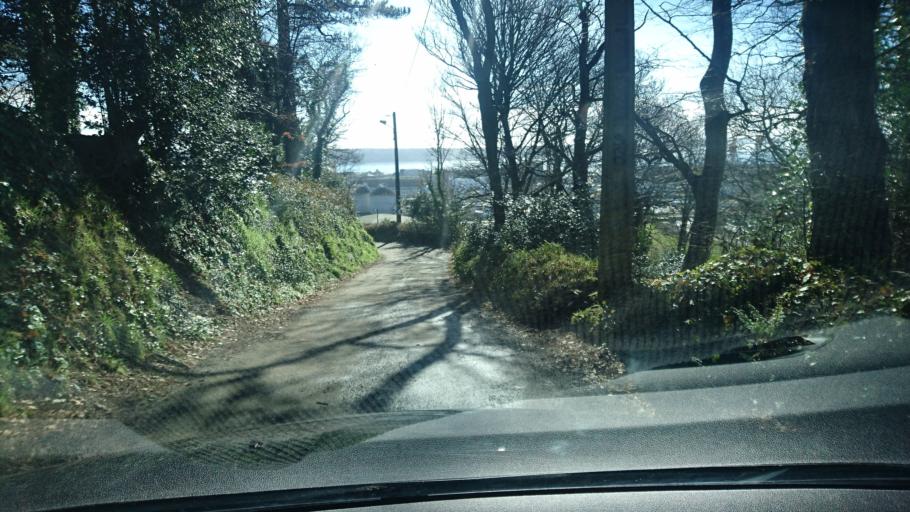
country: FR
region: Brittany
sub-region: Departement du Finistere
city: Brest
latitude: 48.3936
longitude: -4.4534
